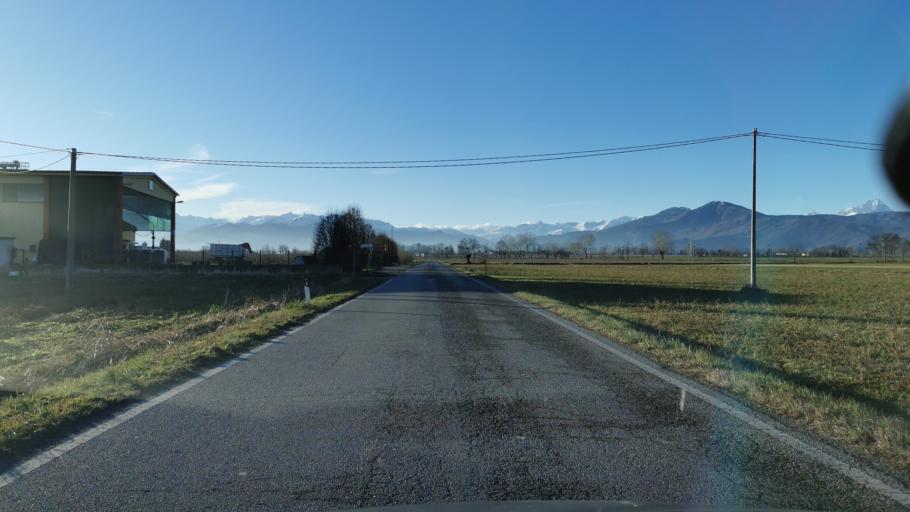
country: IT
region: Piedmont
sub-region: Provincia di Cuneo
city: Roata Rossi
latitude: 44.4579
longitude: 7.5087
